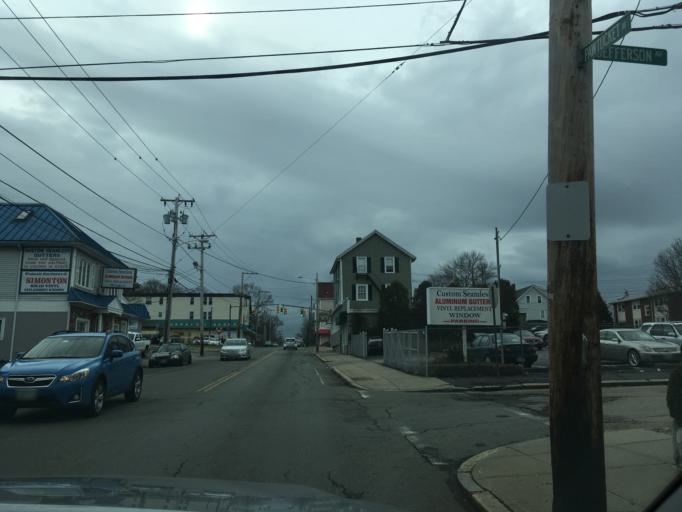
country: US
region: Rhode Island
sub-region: Providence County
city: Pawtucket
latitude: 41.8684
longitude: -71.3895
